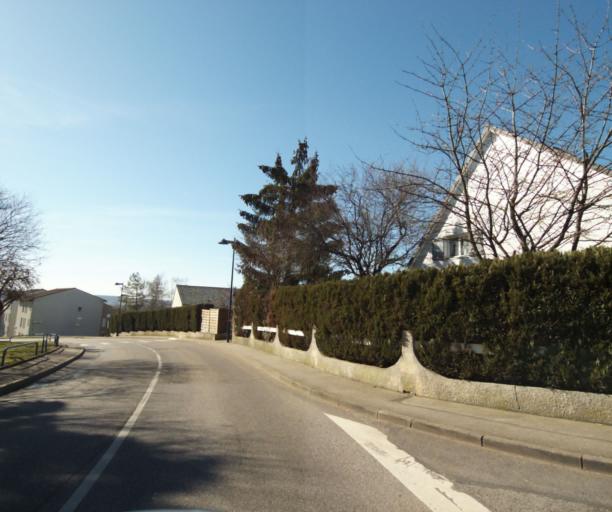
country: FR
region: Lorraine
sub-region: Departement de Meurthe-et-Moselle
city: Ludres
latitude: 48.6156
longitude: 6.1643
